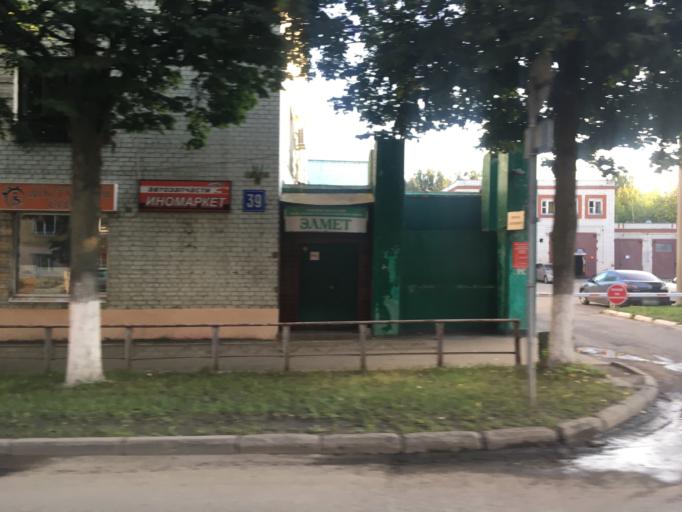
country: RU
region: Mariy-El
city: Yoshkar-Ola
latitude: 56.6462
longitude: 47.8896
